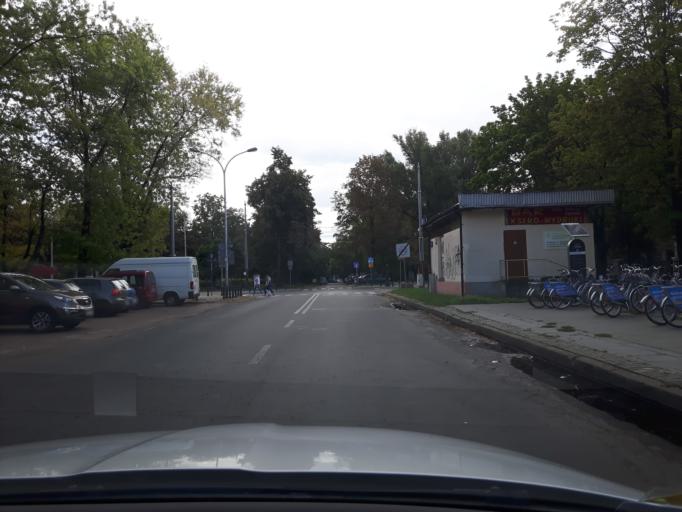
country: PL
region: Masovian Voivodeship
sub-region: Warszawa
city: Praga Polnoc
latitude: 52.2585
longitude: 21.0585
